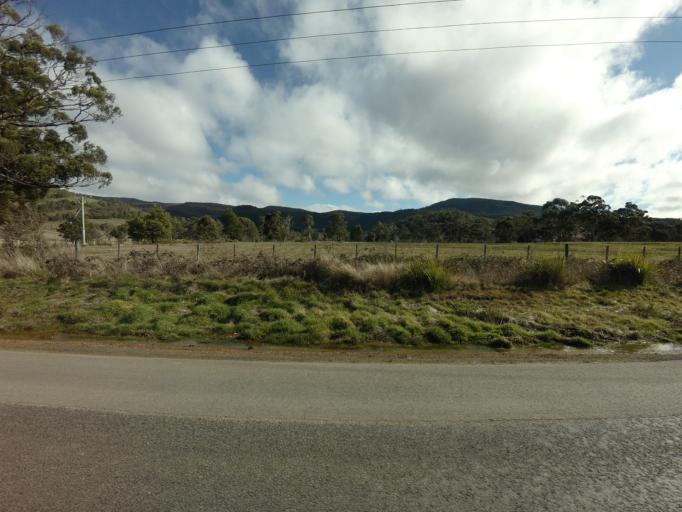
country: AU
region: Tasmania
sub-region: Derwent Valley
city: New Norfolk
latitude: -42.6039
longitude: 146.7062
